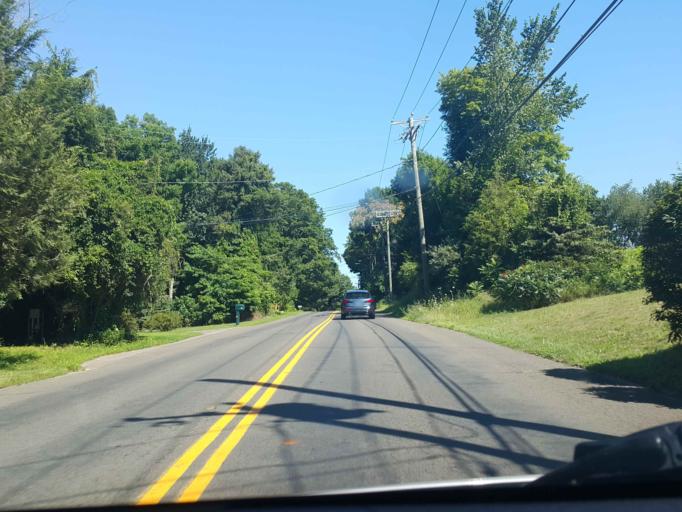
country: US
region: Connecticut
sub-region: New Haven County
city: Guilford
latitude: 41.3008
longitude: -72.6984
